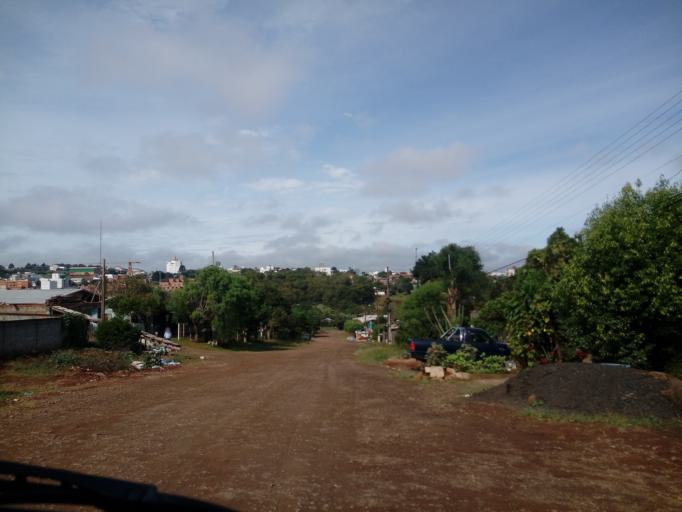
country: BR
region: Santa Catarina
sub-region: Chapeco
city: Chapeco
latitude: -27.0839
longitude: -52.6045
